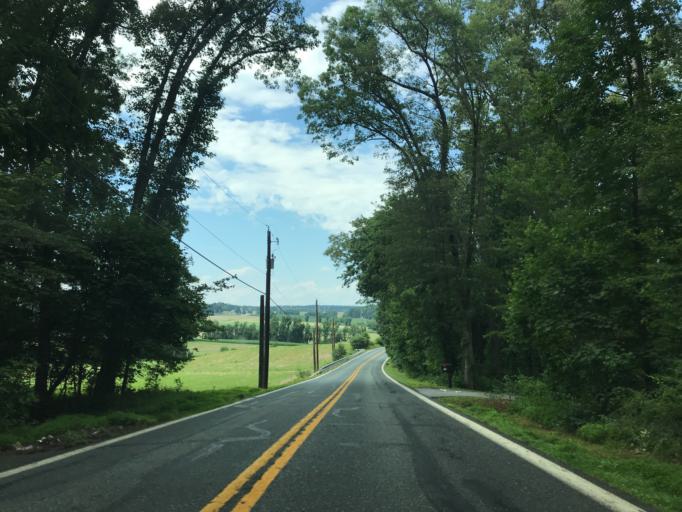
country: US
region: Pennsylvania
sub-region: York County
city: Susquehanna Trails
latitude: 39.6767
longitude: -76.4100
